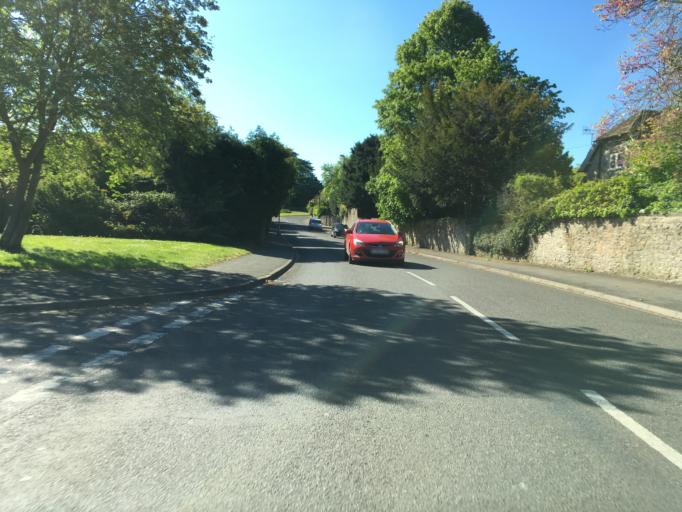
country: GB
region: England
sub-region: South Gloucestershire
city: Severn Beach
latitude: 51.5078
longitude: -2.6351
